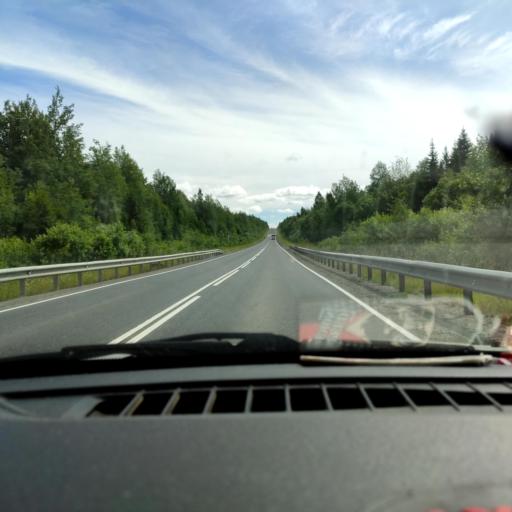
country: RU
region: Perm
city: Chusovoy
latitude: 58.3732
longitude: 57.9863
